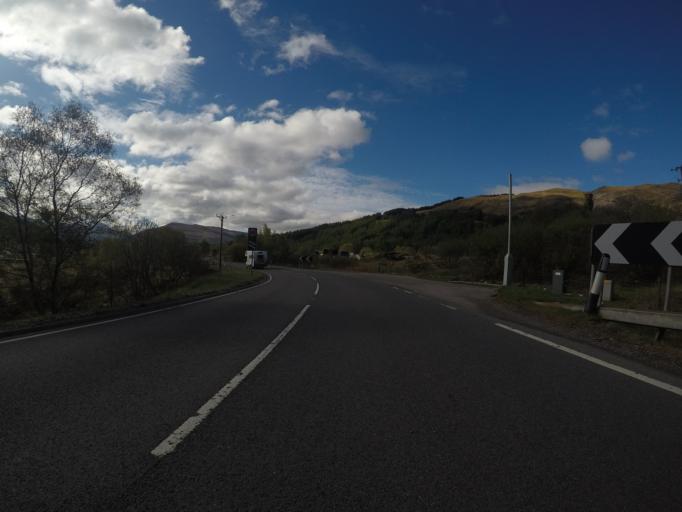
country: GB
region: Scotland
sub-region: Argyll and Bute
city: Garelochhead
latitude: 56.4400
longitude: -4.7180
